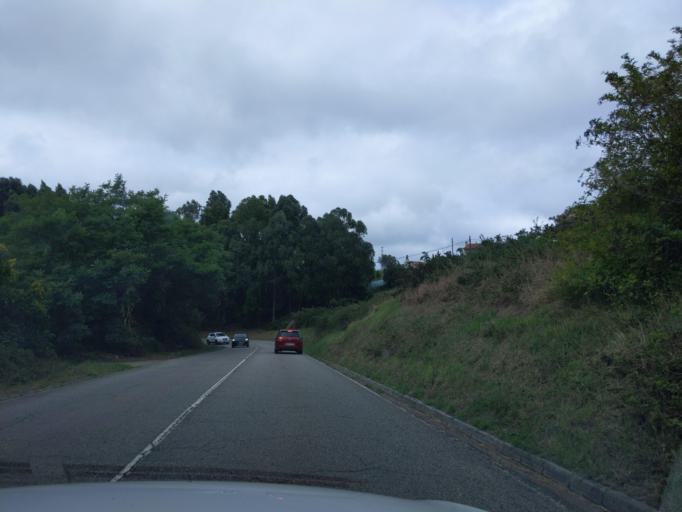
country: ES
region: Asturias
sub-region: Province of Asturias
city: Aviles
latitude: 43.5860
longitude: -5.9125
